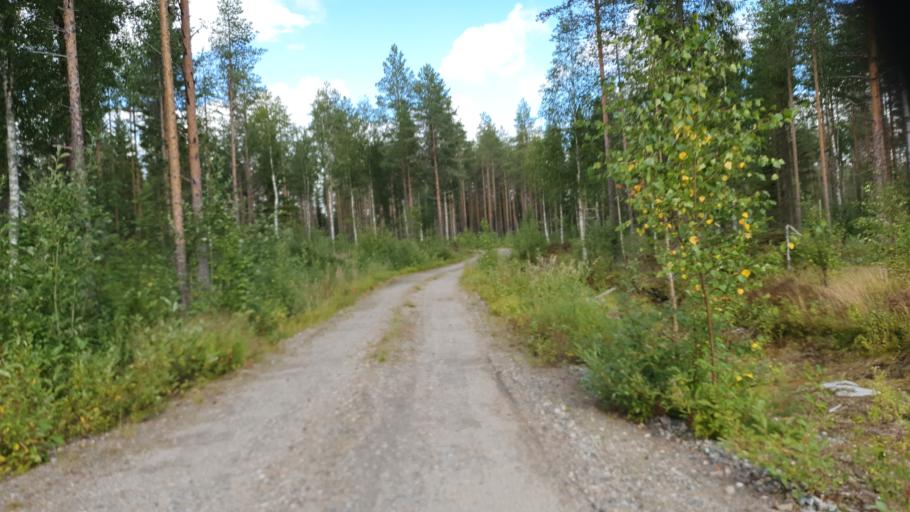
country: FI
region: Kainuu
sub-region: Kehys-Kainuu
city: Kuhmo
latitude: 64.1423
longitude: 29.3870
